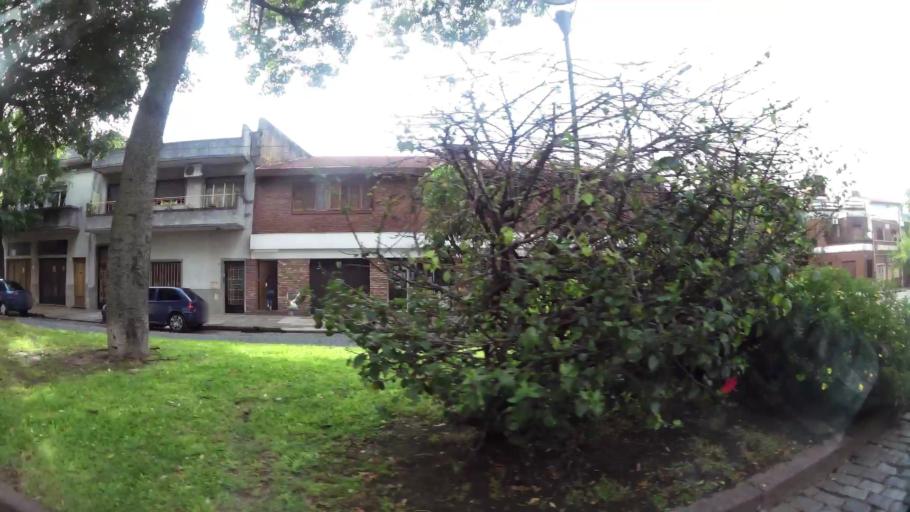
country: AR
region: Buenos Aires F.D.
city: Villa Santa Rita
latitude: -34.6409
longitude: -58.4684
